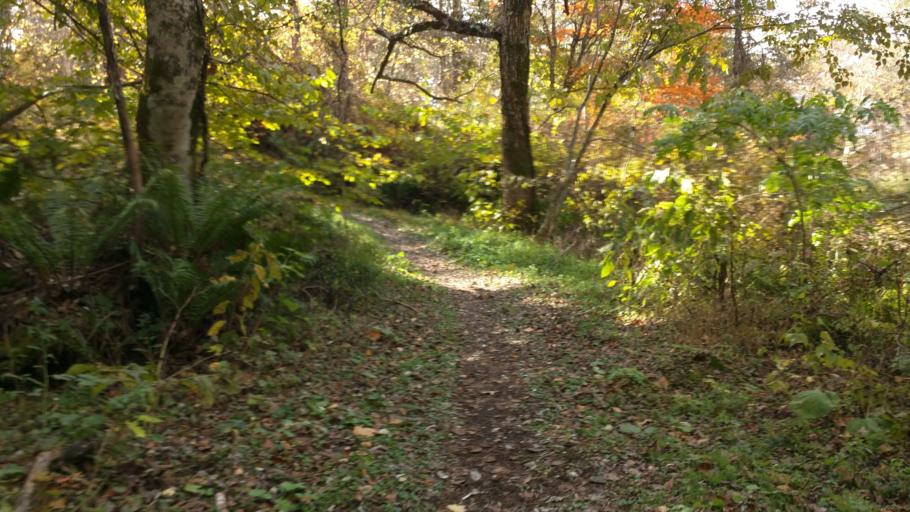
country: JP
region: Fukushima
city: Inawashiro
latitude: 37.6524
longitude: 140.0710
